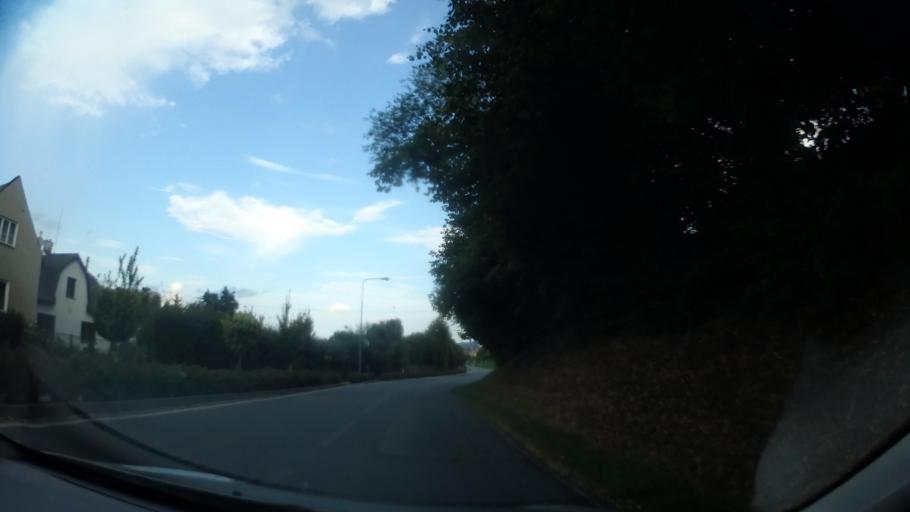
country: CZ
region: Olomoucky
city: Zabreh
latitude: 49.8852
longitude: 16.8562
